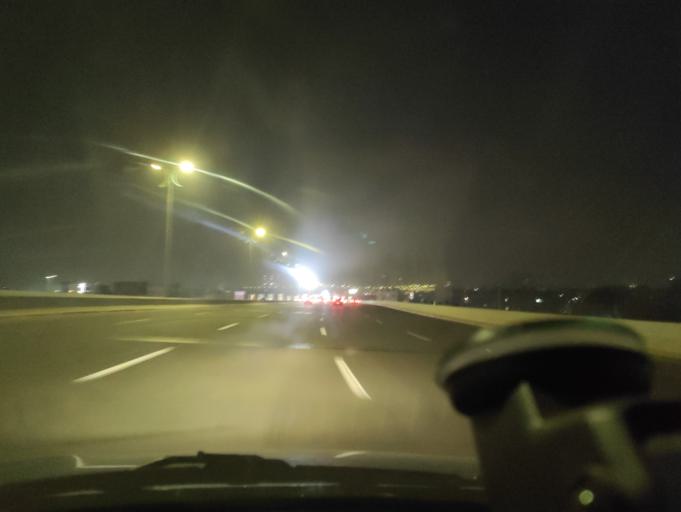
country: EG
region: Muhafazat al Qahirah
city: Cairo
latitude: 30.1122
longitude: 31.2220
